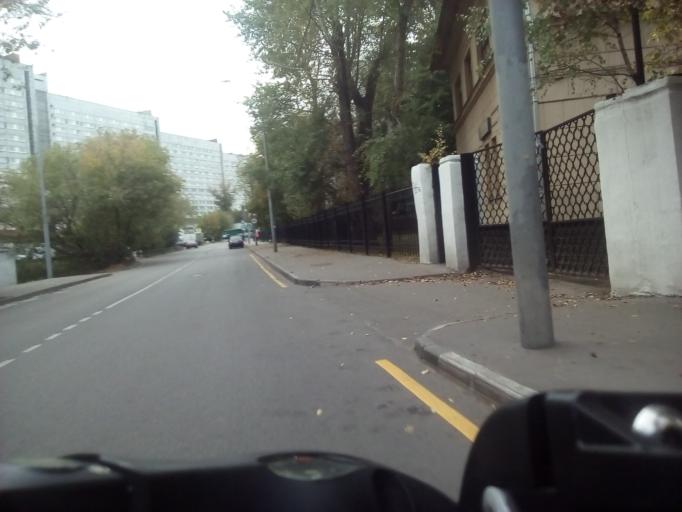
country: RU
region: Moscow
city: Rostokino
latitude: 55.8247
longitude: 37.6587
